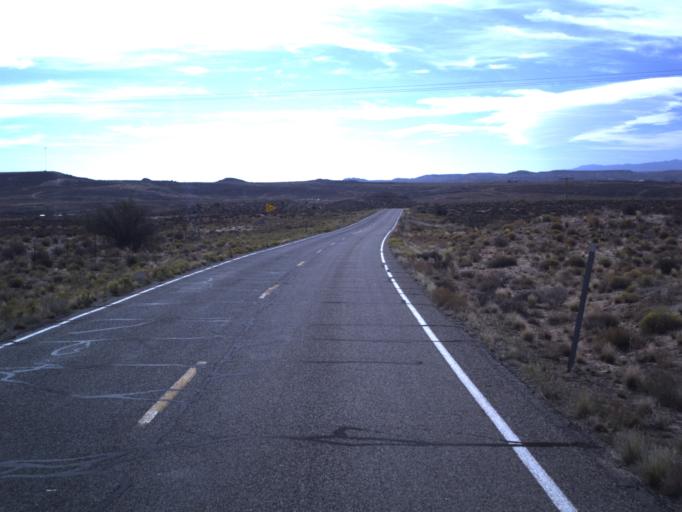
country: US
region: Utah
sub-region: San Juan County
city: Blanding
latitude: 37.3167
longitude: -109.3070
